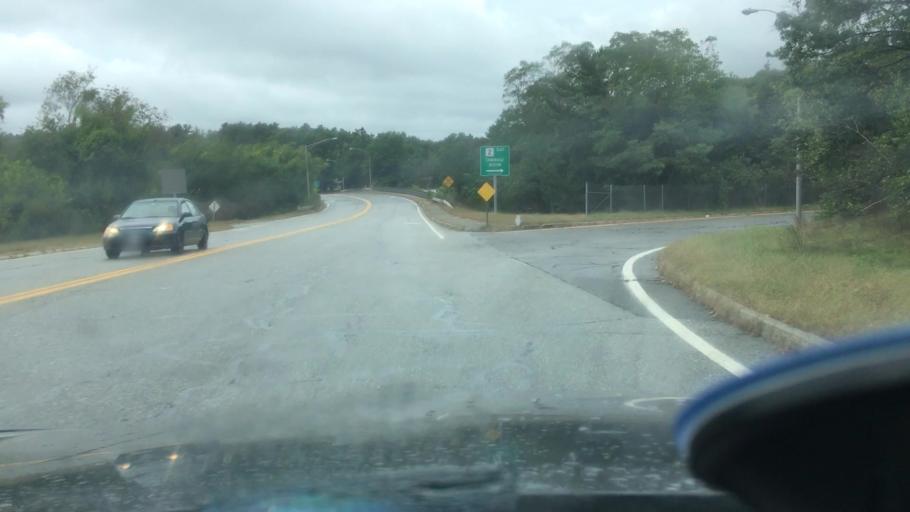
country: US
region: Massachusetts
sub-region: Middlesex County
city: Belmont
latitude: 42.4161
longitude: -71.2042
